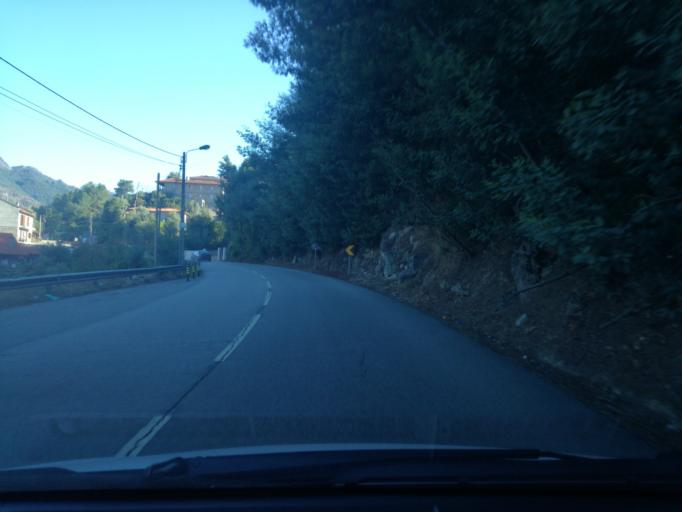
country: PT
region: Braga
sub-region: Vieira do Minho
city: Real
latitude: 41.6841
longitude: -8.1717
